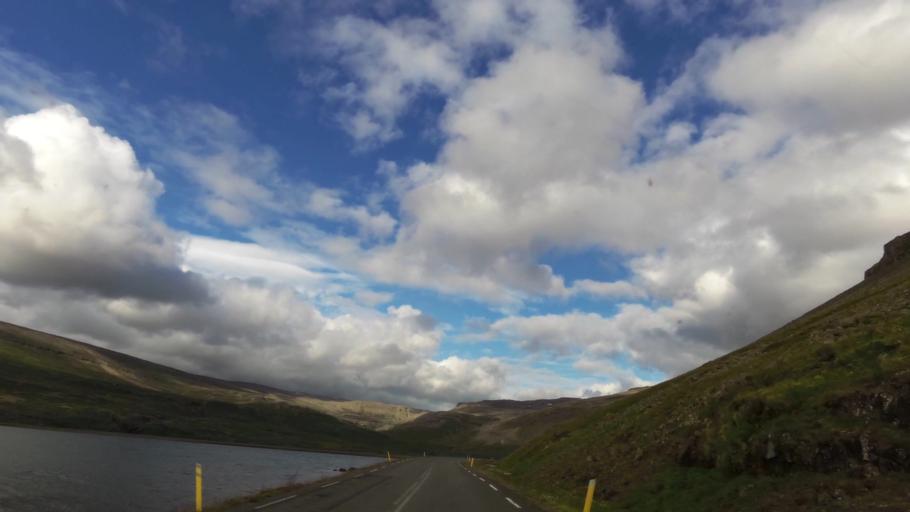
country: IS
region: West
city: Olafsvik
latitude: 65.5301
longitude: -23.7995
